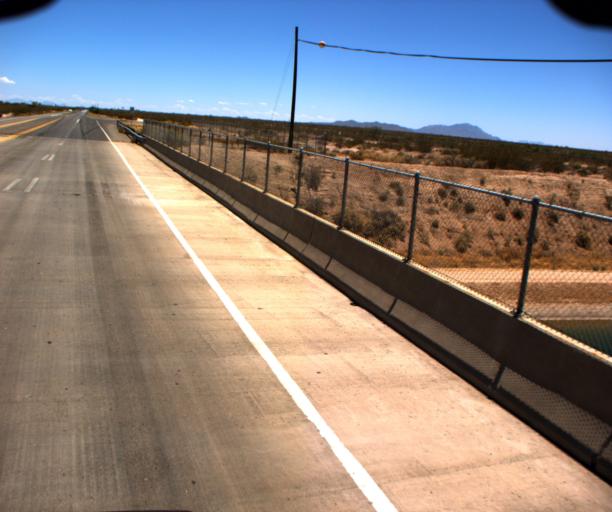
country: US
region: Arizona
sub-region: Pinal County
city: Florence
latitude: 33.0098
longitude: -111.3768
